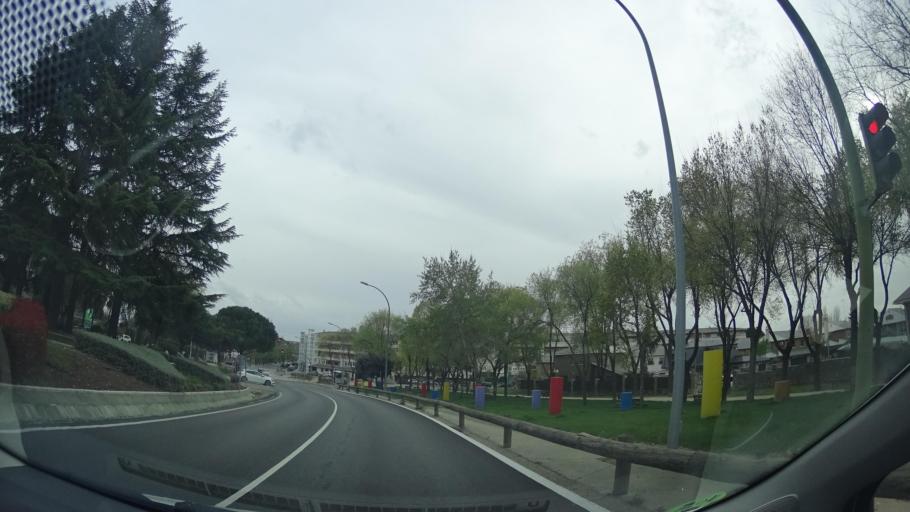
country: ES
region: Madrid
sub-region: Provincia de Madrid
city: Colmenar Viejo
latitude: 40.6739
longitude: -3.7702
